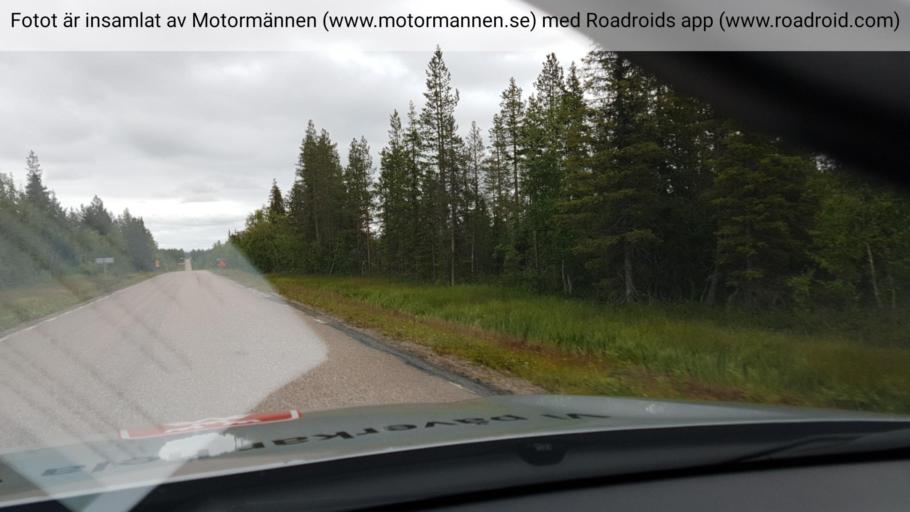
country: SE
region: Norrbotten
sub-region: Overkalix Kommun
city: OEverkalix
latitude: 67.0451
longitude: 22.0703
